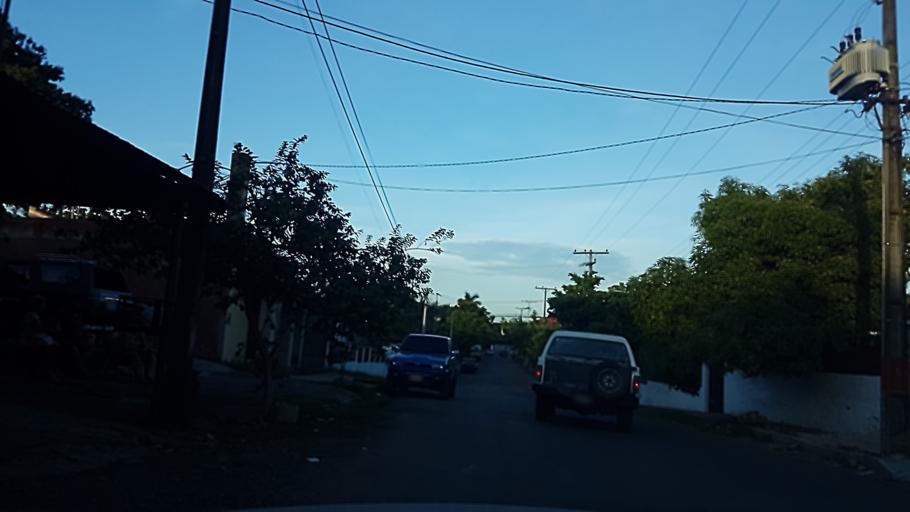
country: PY
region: Asuncion
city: Asuncion
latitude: -25.2682
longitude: -57.5880
